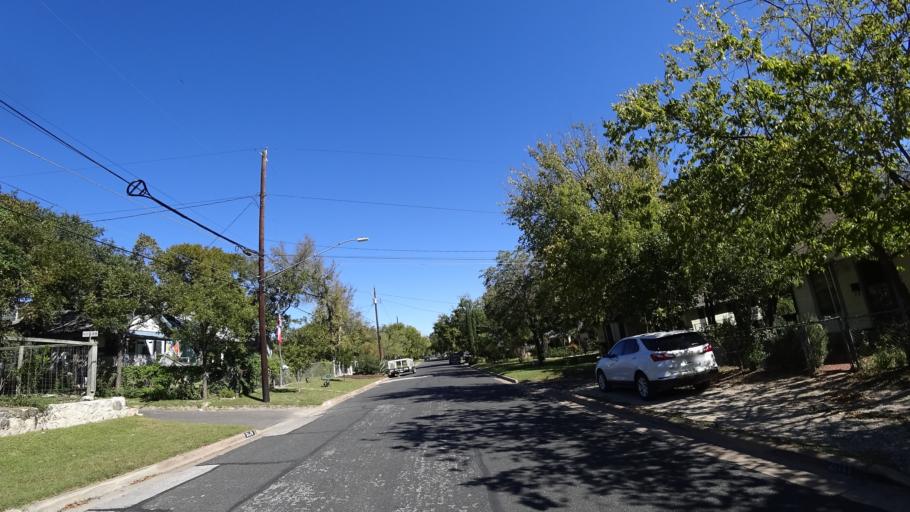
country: US
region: Texas
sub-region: Travis County
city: Austin
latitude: 30.2456
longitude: -97.7603
